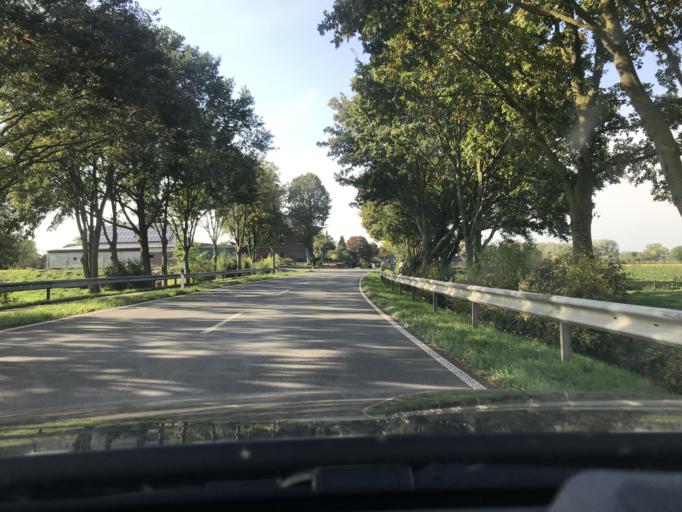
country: DE
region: North Rhine-Westphalia
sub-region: Regierungsbezirk Dusseldorf
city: Emmerich
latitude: 51.8038
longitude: 6.2101
